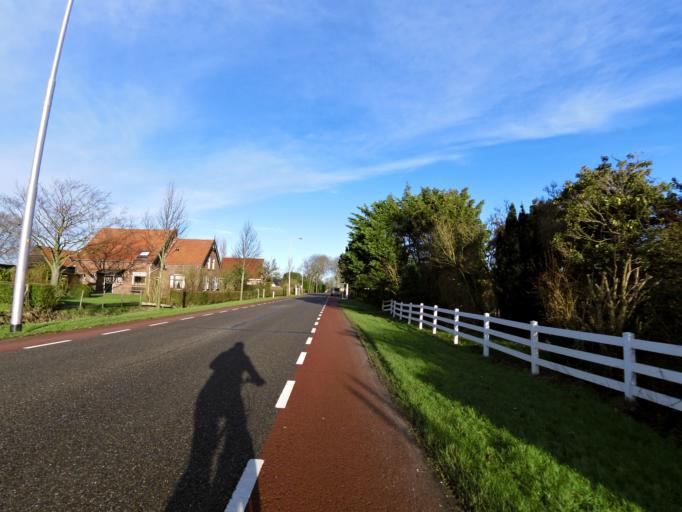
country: NL
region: South Holland
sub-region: Gemeente Hellevoetsluis
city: Nieuwenhoorn
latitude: 51.8903
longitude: 4.0876
